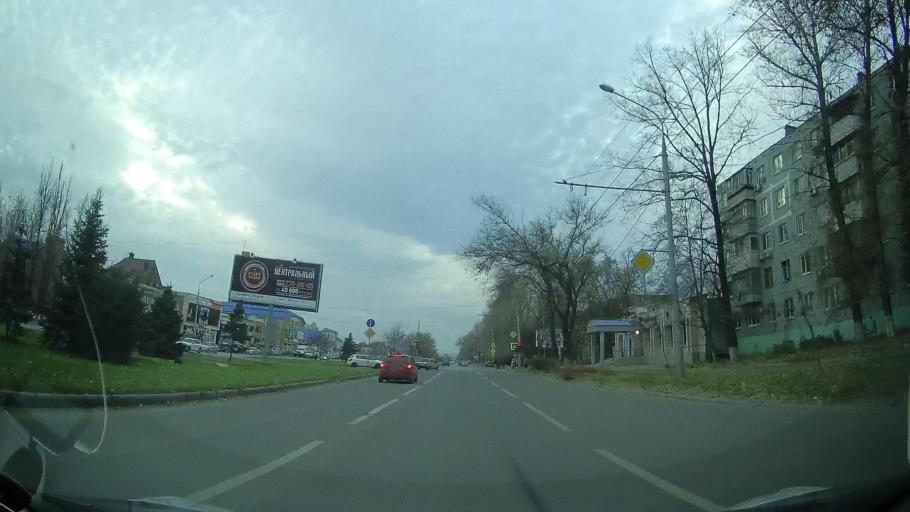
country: RU
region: Rostov
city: Aksay
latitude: 47.2380
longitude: 39.8229
